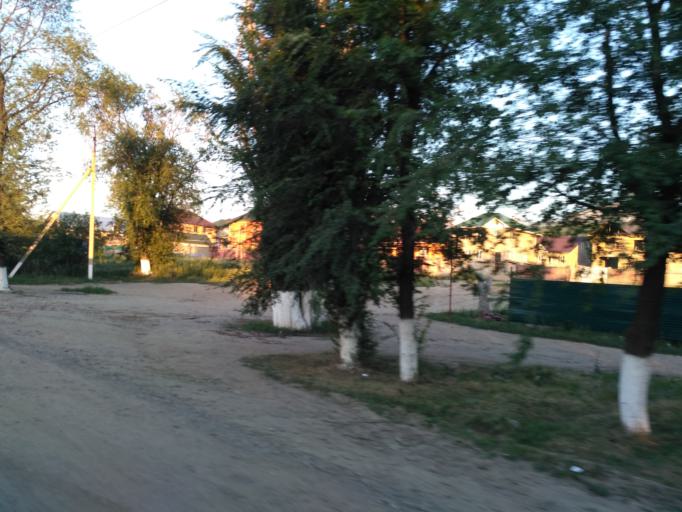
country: KZ
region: Almaty Qalasy
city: Almaty
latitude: 43.1736
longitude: 76.7821
